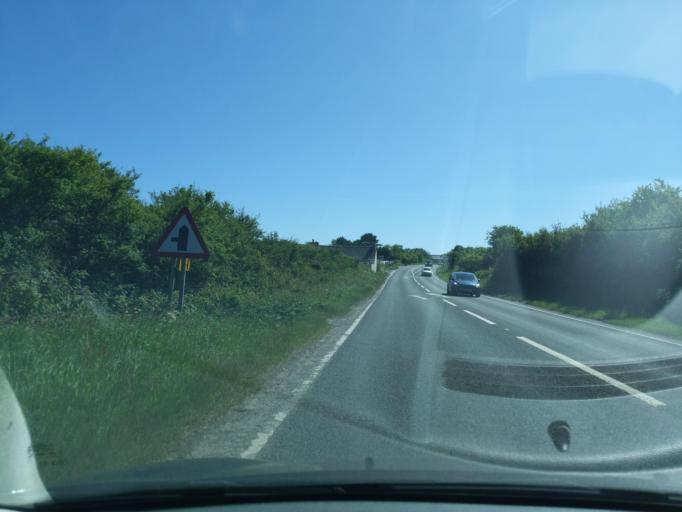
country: GB
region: England
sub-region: Cornwall
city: Wendron
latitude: 50.1369
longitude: -5.2202
